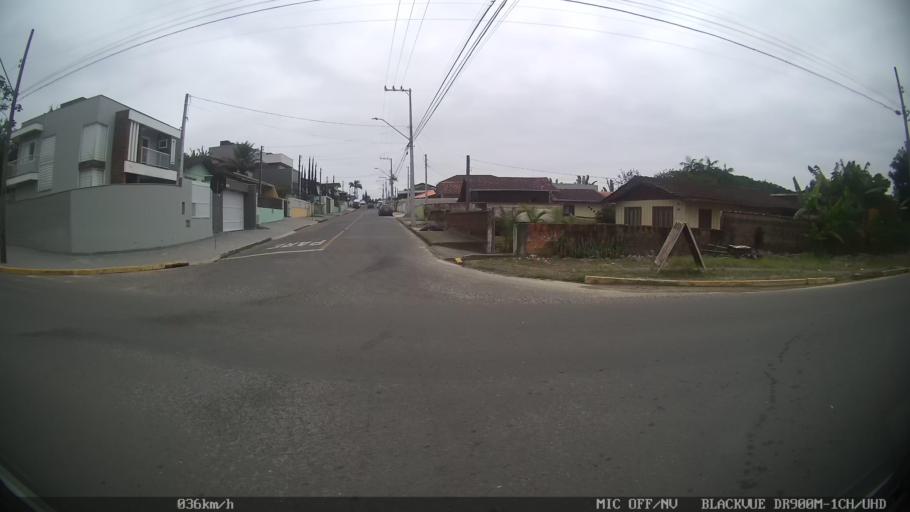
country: BR
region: Santa Catarina
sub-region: Joinville
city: Joinville
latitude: -26.3543
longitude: -48.8387
